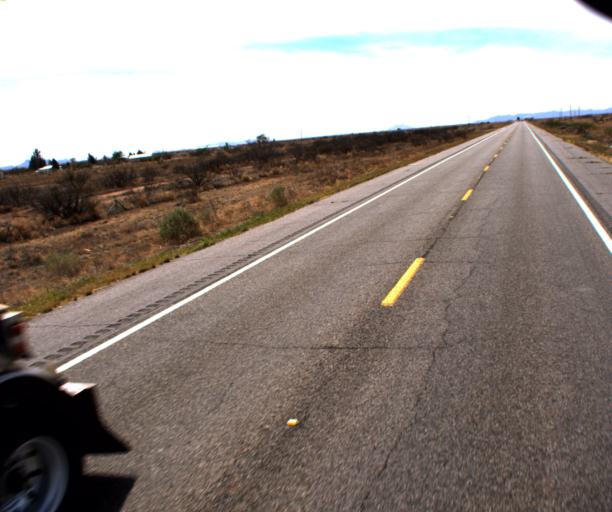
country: US
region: Arizona
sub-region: Cochise County
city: Pirtleville
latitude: 31.5739
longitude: -109.6683
